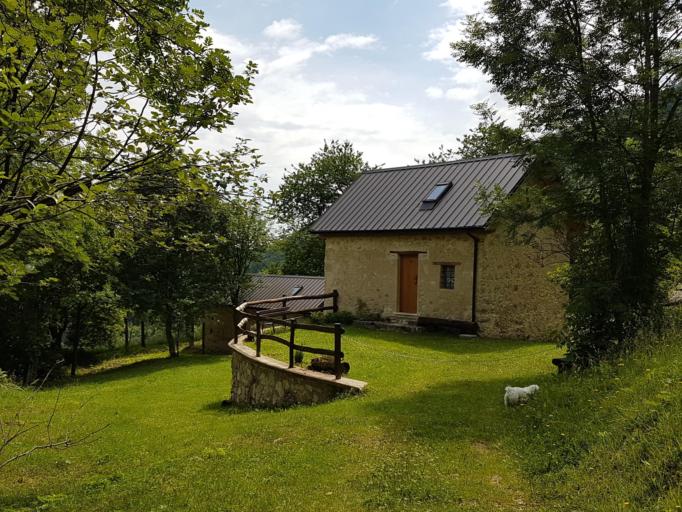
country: IT
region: Veneto
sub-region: Provincia di Vicenza
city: Recoaro Terme
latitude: 45.6783
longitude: 11.2005
